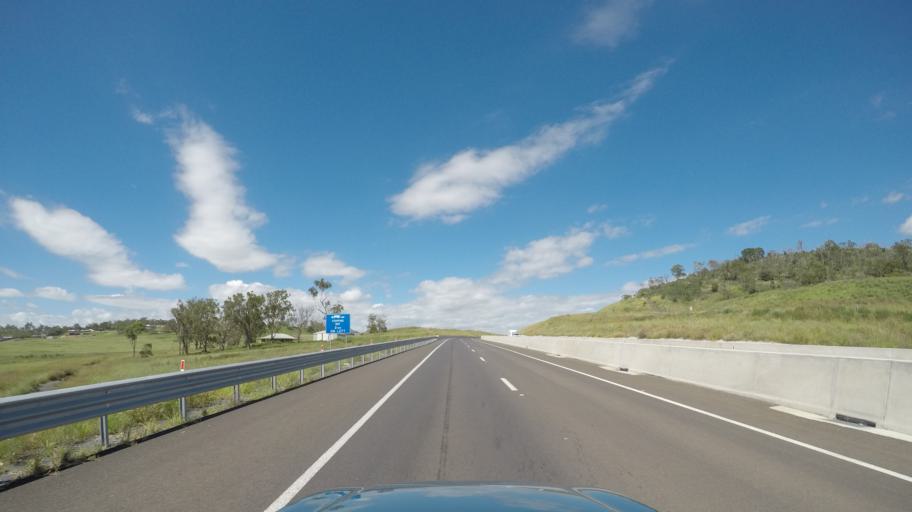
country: AU
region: Queensland
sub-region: Toowoomba
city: Wilsonton Heights
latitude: -27.5104
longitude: 151.8992
